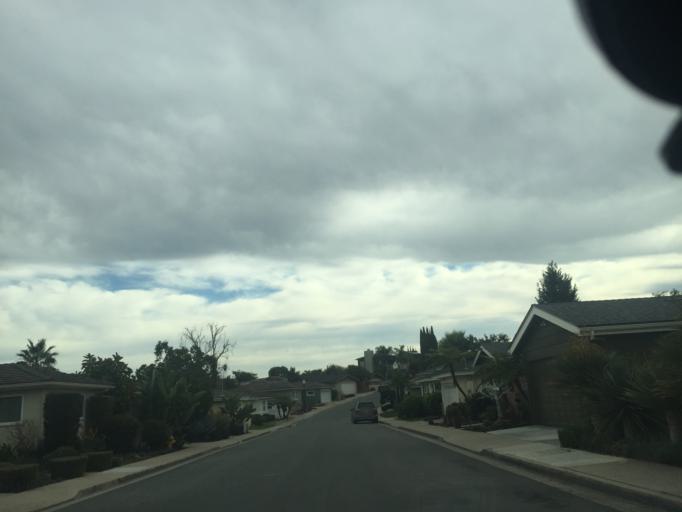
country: US
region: California
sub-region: San Diego County
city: Lemon Grove
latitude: 32.7698
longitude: -117.0943
